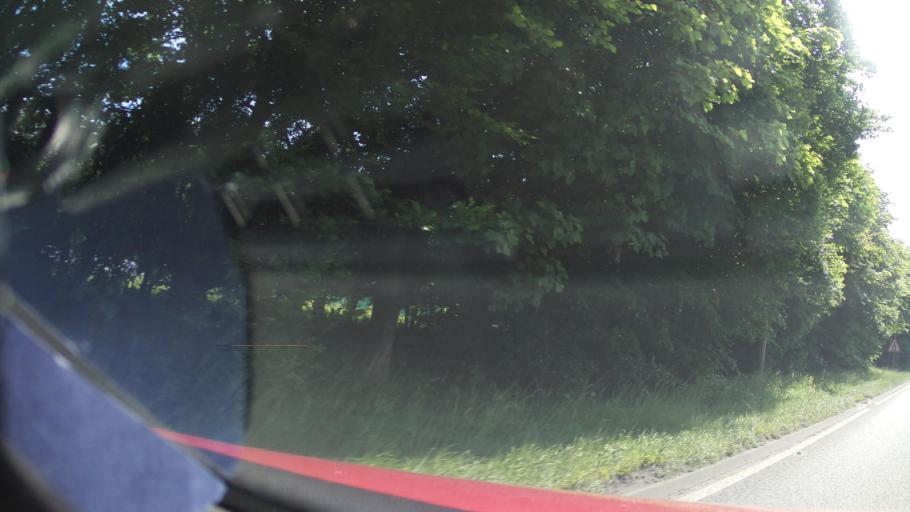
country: GB
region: England
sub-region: North Lincolnshire
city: Broughton
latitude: 53.5537
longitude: -0.5790
